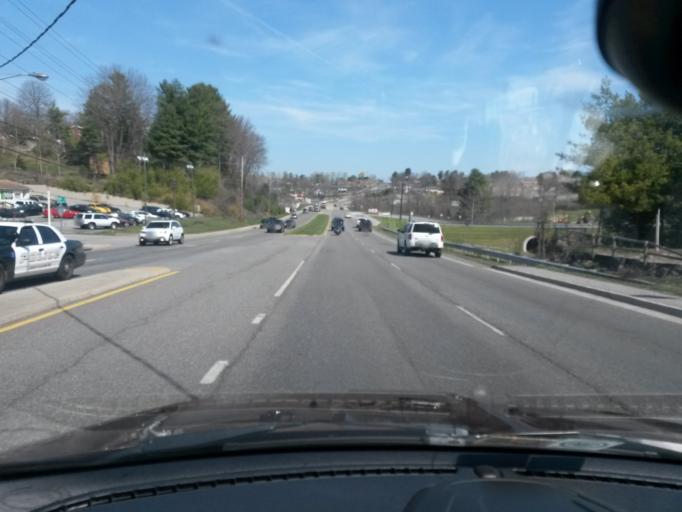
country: US
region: Virginia
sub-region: Montgomery County
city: Christiansburg
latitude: 37.1369
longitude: -80.4140
